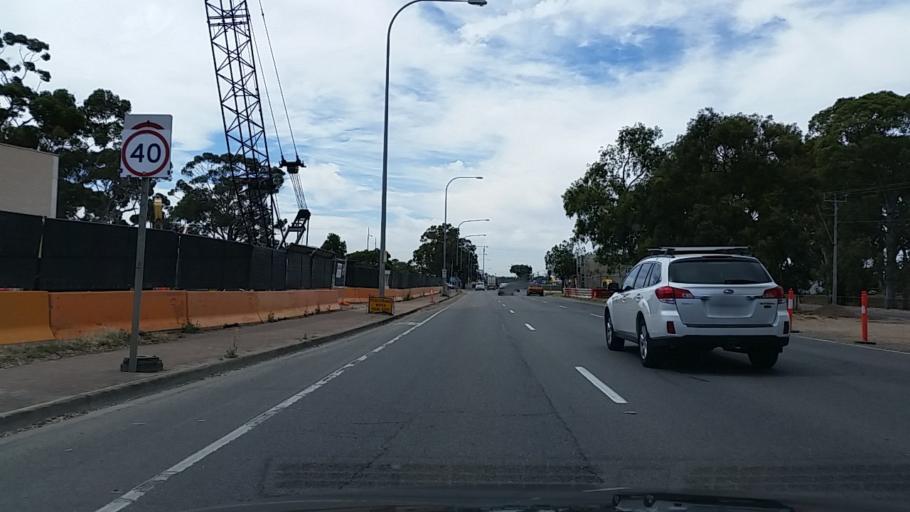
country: AU
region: South Australia
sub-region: Marion
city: Clovelly Park
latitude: -35.0093
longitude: 138.5759
